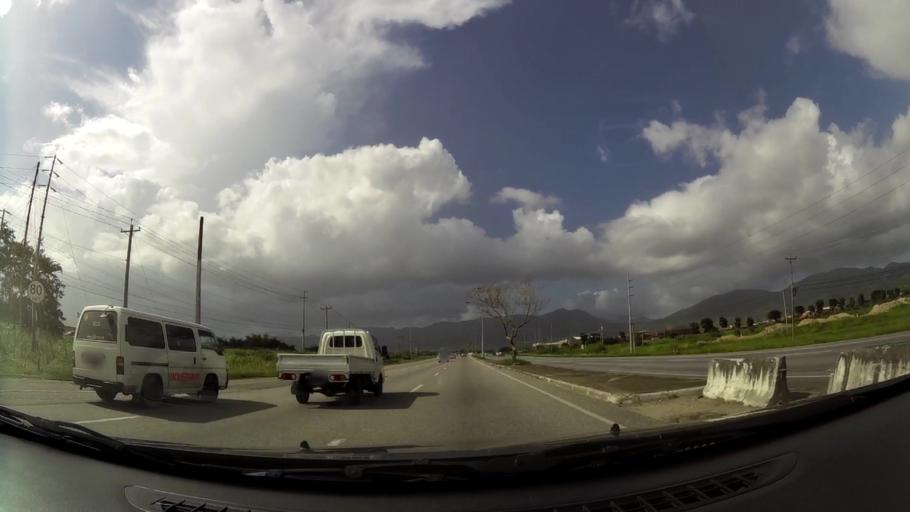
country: TT
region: Tunapuna/Piarco
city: Arouca
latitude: 10.6212
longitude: -61.3537
